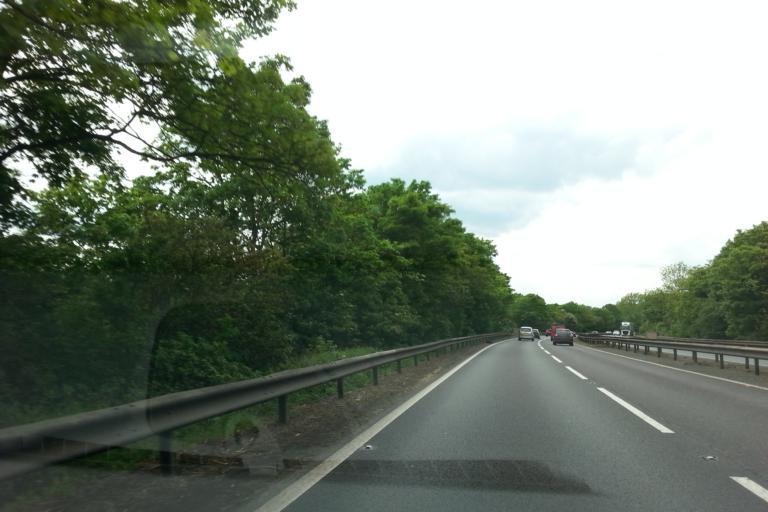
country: GB
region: England
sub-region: Peterborough
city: Wansford
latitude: 52.5671
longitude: -0.3913
